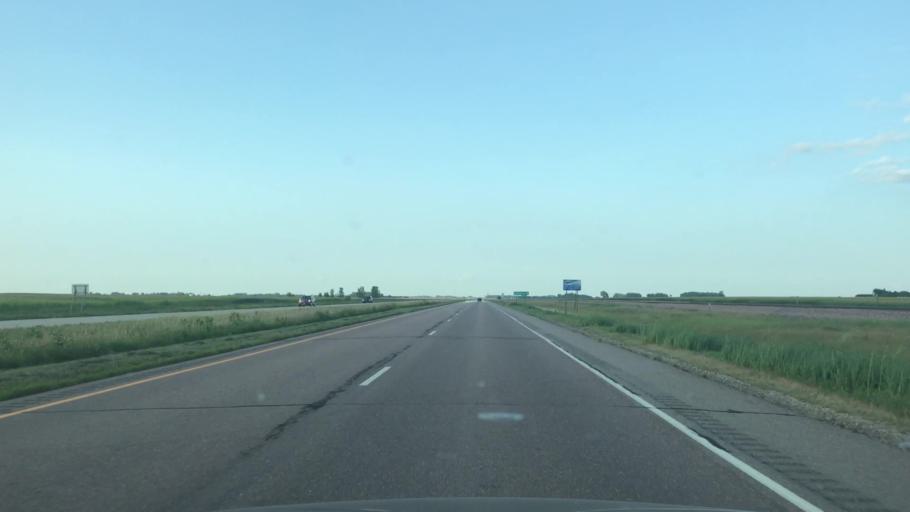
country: US
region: Minnesota
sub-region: Nobles County
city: Worthington
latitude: 43.7280
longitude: -95.4263
